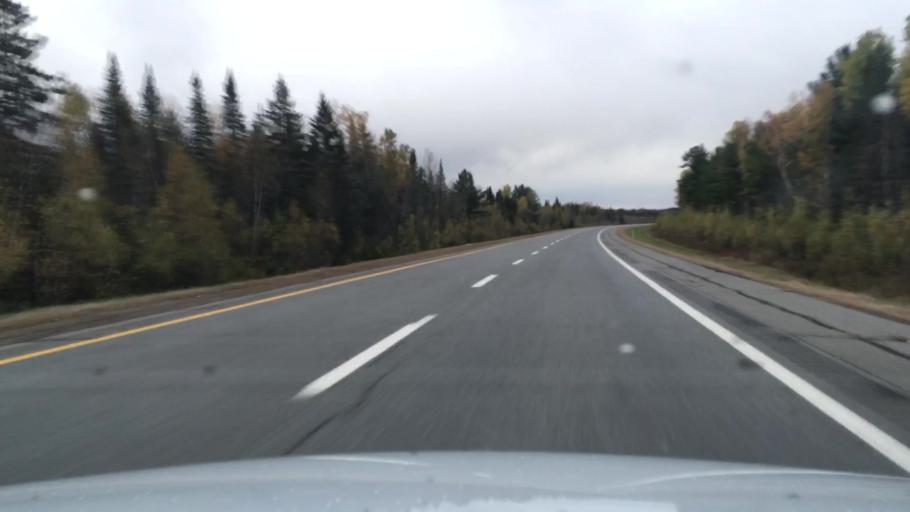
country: US
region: Maine
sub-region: Penobscot County
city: Greenbush
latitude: 45.1204
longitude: -68.6950
